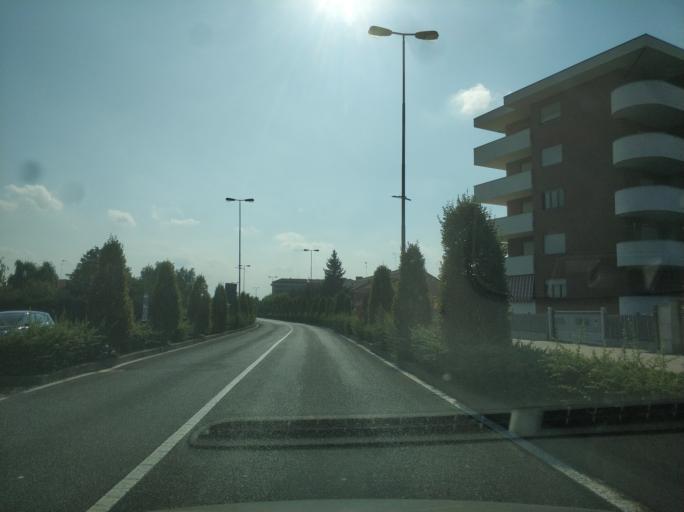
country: IT
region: Piedmont
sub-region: Provincia di Cuneo
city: Bra
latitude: 44.7016
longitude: 7.8416
